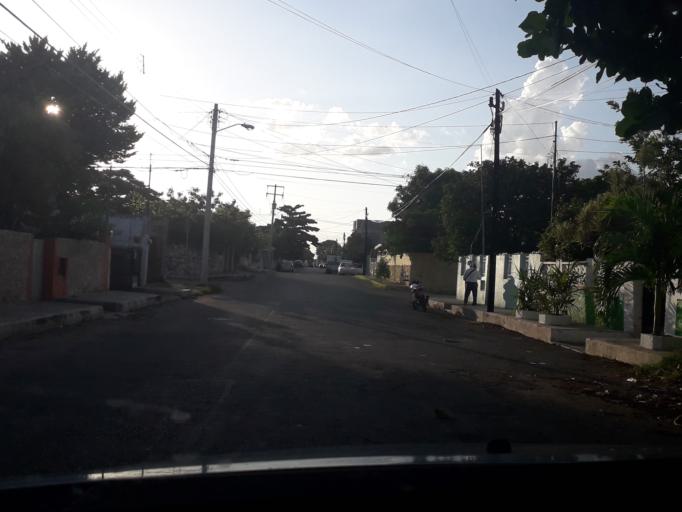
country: MX
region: Yucatan
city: Merida
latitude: 20.9800
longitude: -89.6519
